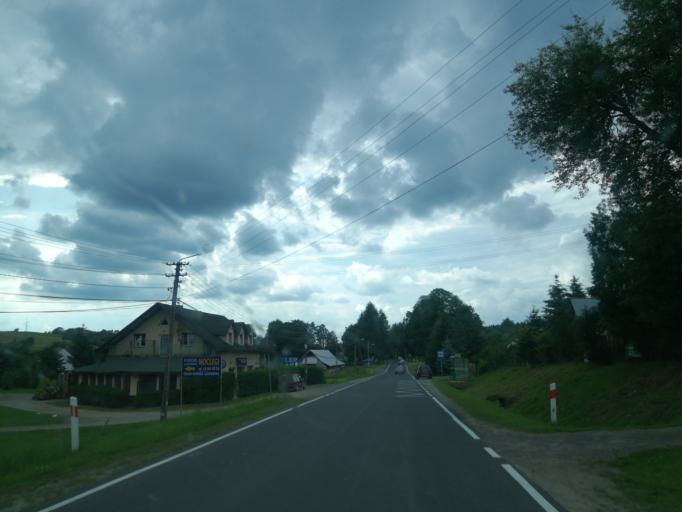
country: PL
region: Subcarpathian Voivodeship
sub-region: Powiat leski
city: Olszanica
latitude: 49.4438
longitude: 22.4482
